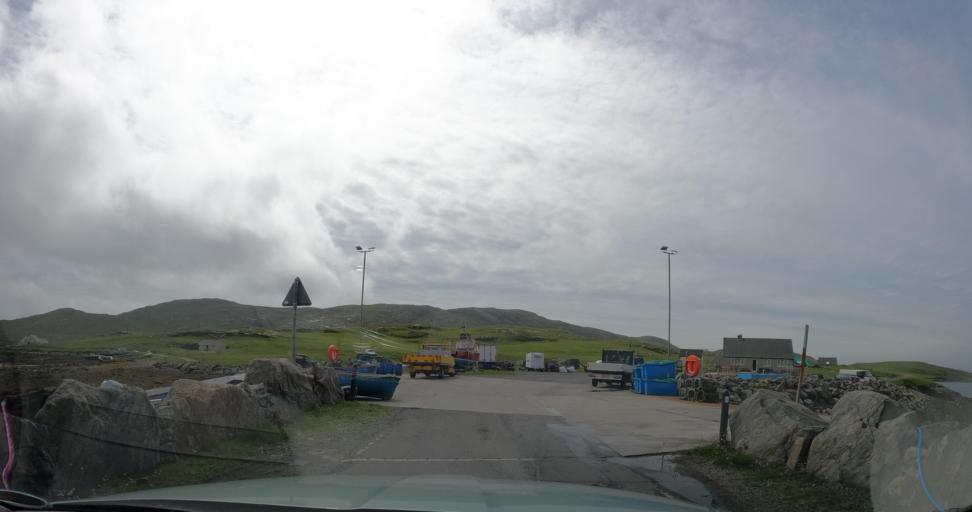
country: GB
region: Scotland
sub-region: Eilean Siar
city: Barra
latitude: 56.9461
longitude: -7.5329
